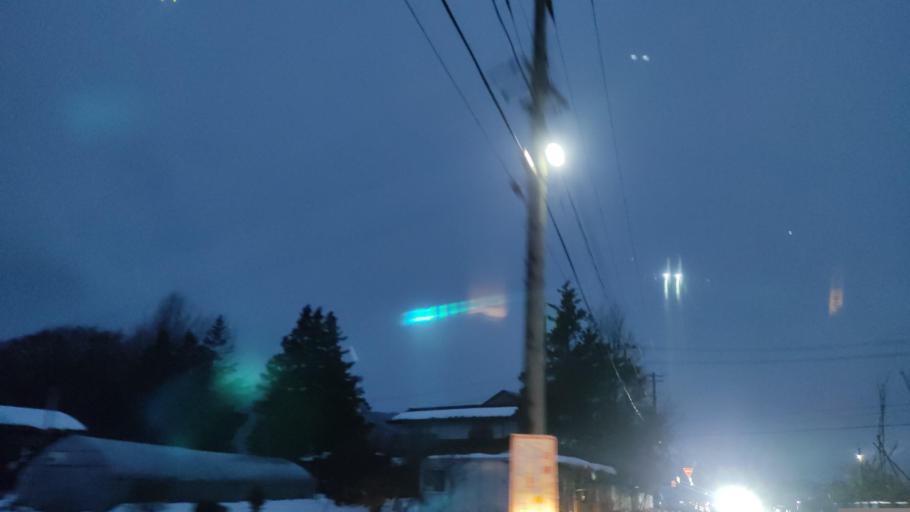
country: JP
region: Iwate
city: Morioka-shi
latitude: 39.6317
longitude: 141.1053
